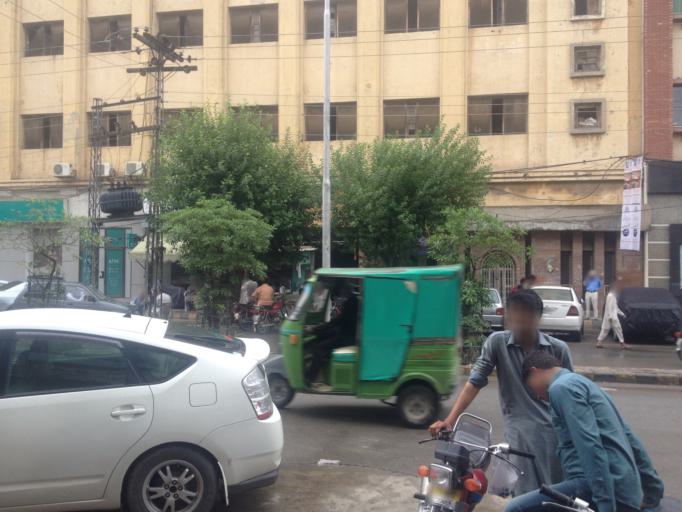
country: PK
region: Punjab
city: Lahore
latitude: 31.5639
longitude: 74.3088
